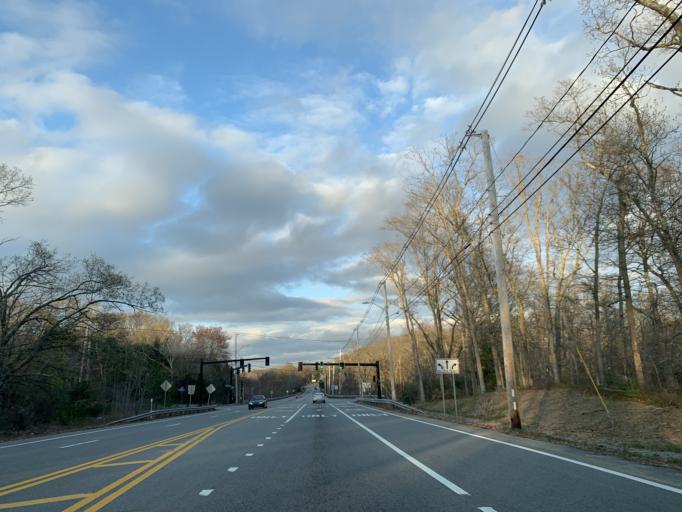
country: US
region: Massachusetts
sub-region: Bristol County
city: North Seekonk
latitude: 41.9324
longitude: -71.3294
